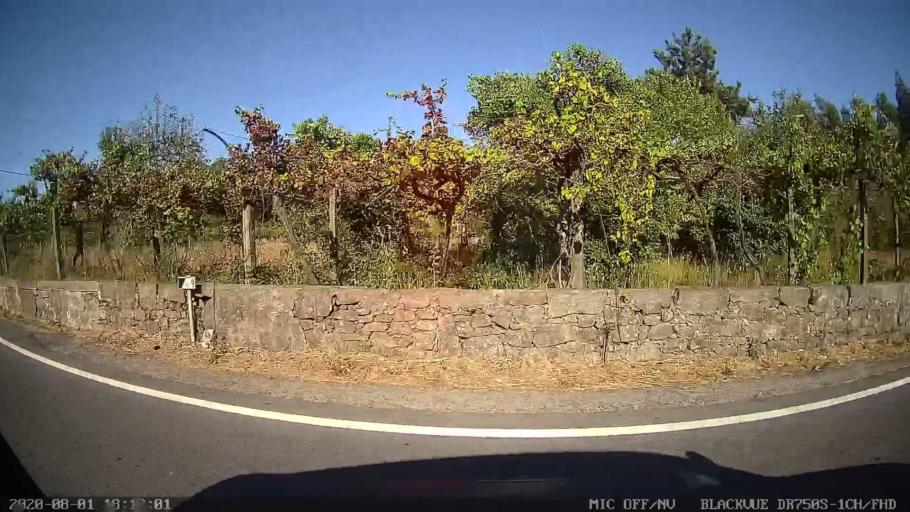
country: PT
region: Porto
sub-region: Santo Tirso
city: Sao Miguel do Couto
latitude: 41.2938
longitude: -8.4710
